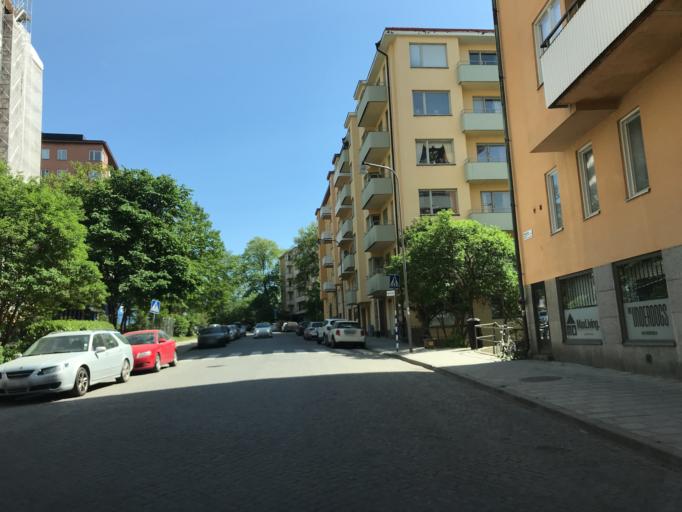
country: SE
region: Stockholm
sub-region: Stockholms Kommun
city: OEstermalm
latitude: 59.3458
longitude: 18.0982
